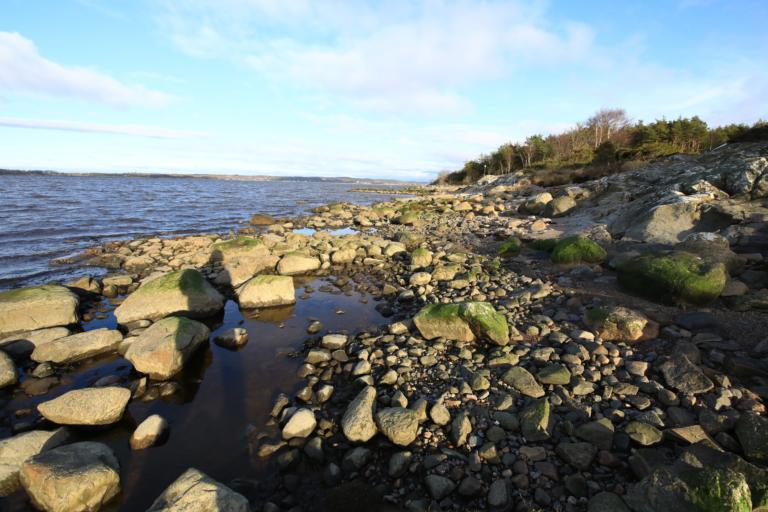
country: SE
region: Halland
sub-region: Varbergs Kommun
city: Varberg
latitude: 57.2040
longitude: 12.1936
